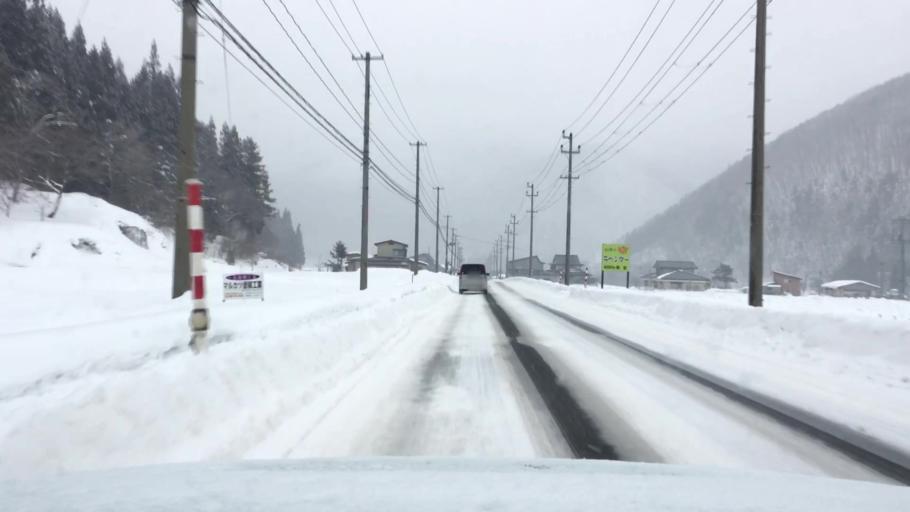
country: JP
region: Akita
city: Hanawa
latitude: 40.0729
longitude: 141.0195
